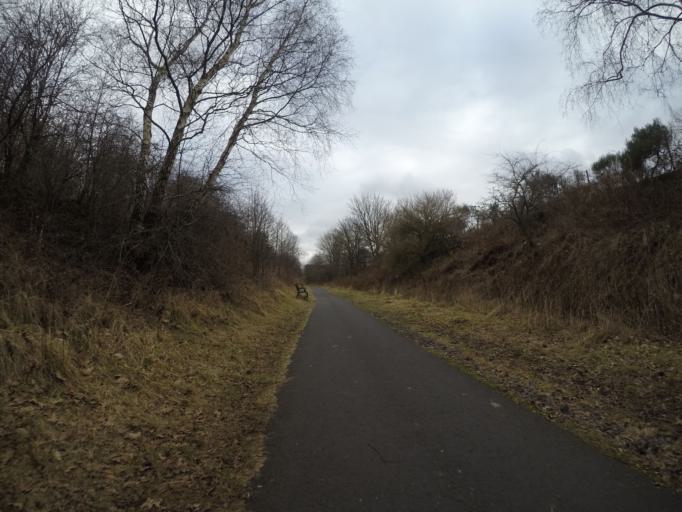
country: GB
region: Scotland
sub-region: North Ayrshire
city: Dreghorn
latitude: 55.6092
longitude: -4.6331
